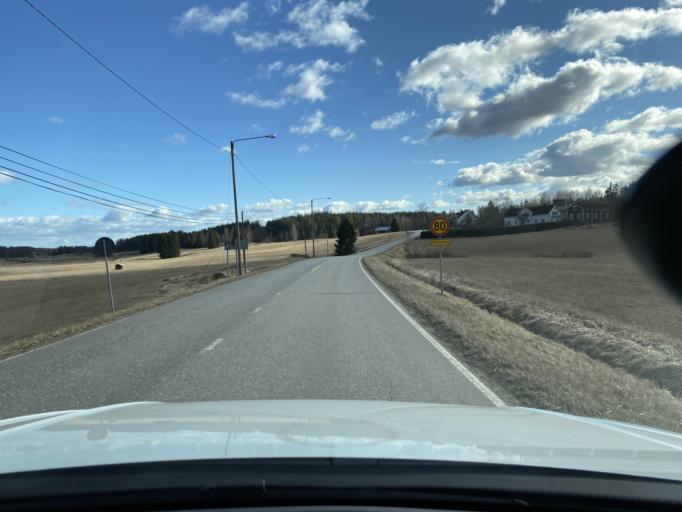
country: FI
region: Pirkanmaa
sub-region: Lounais-Pirkanmaa
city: Punkalaidun
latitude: 61.0677
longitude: 23.1803
